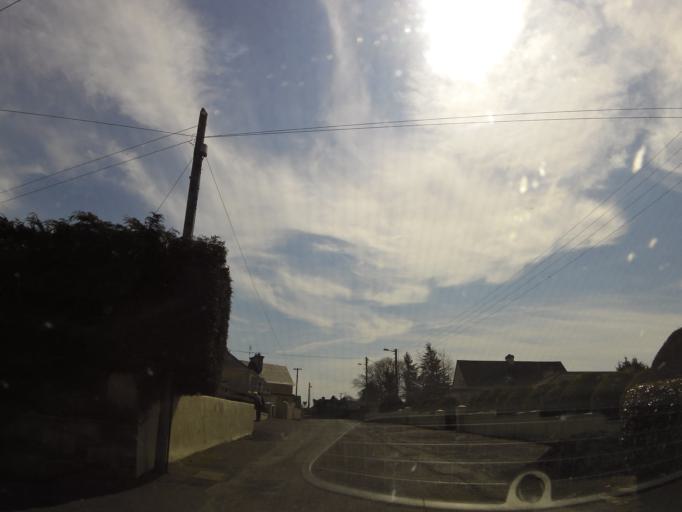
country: IE
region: Connaught
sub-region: Maigh Eo
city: Kiltamagh
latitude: 53.8469
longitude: -9.0026
